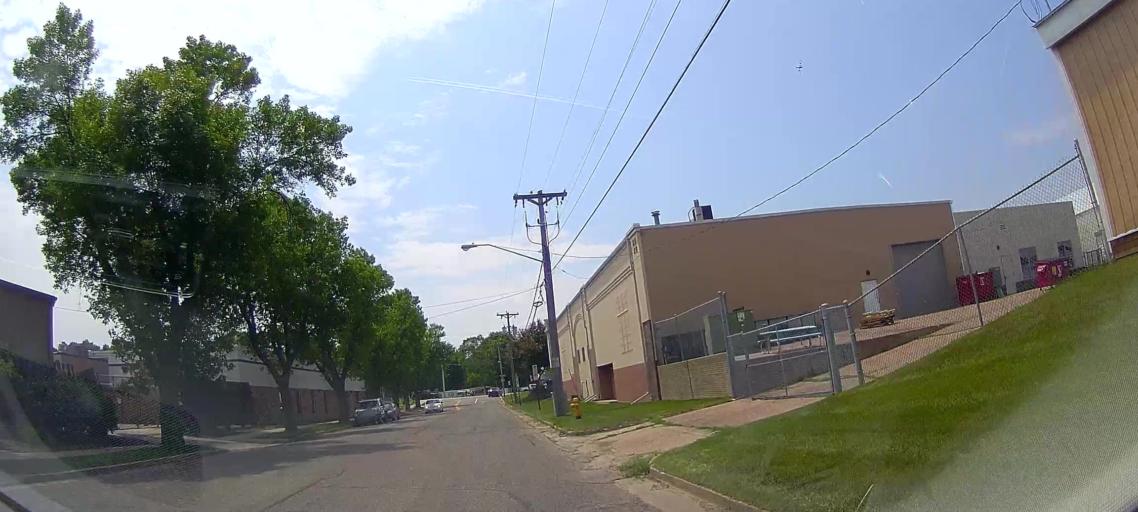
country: US
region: South Dakota
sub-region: Minnehaha County
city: Sioux Falls
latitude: 43.5062
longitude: -96.7487
